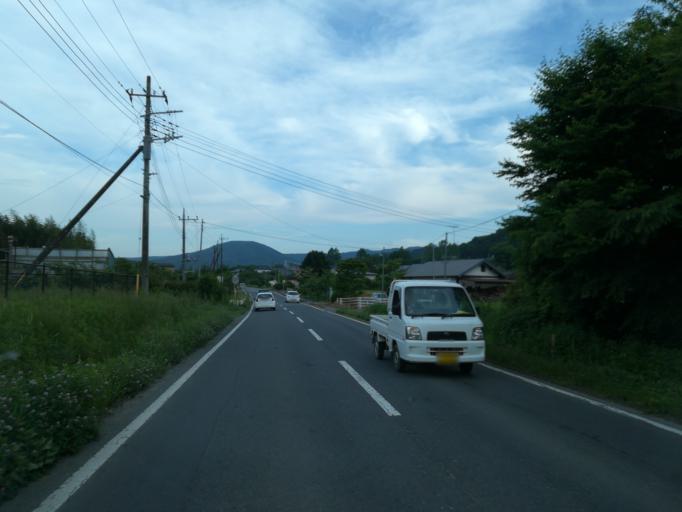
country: JP
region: Ibaraki
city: Tsukuba
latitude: 36.2178
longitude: 140.1688
